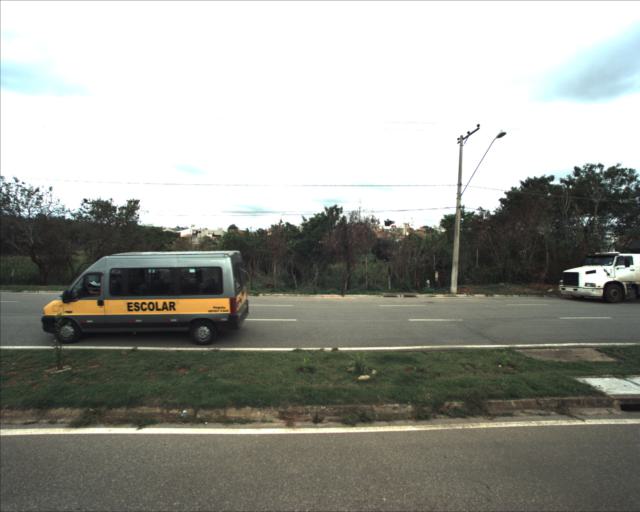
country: BR
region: Sao Paulo
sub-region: Sorocaba
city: Sorocaba
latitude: -23.4328
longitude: -47.5002
